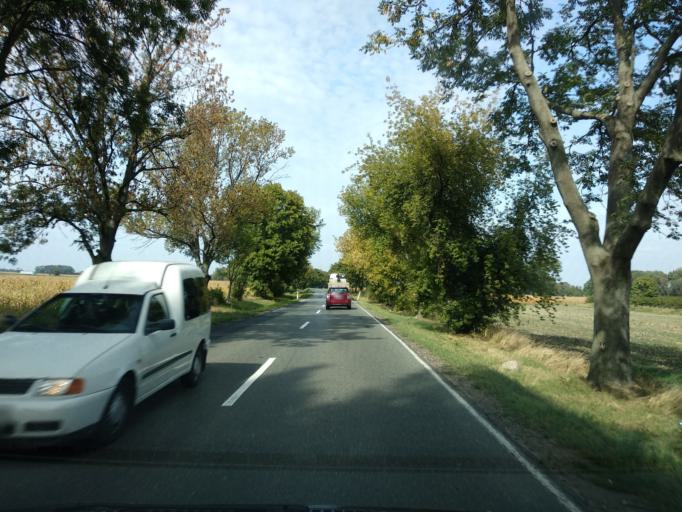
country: PL
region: Lower Silesian Voivodeship
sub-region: Powiat wroclawski
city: Zorawina
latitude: 50.9265
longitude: 17.0698
